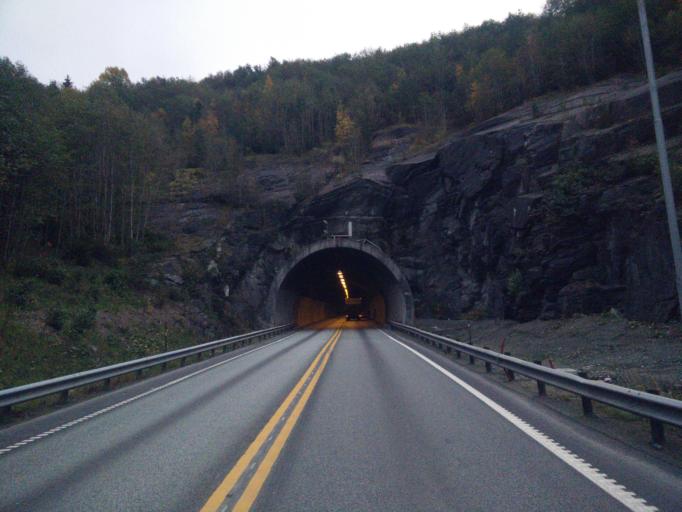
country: NO
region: Sor-Trondelag
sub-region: Malvik
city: Malvik
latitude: 63.4230
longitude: 10.5826
